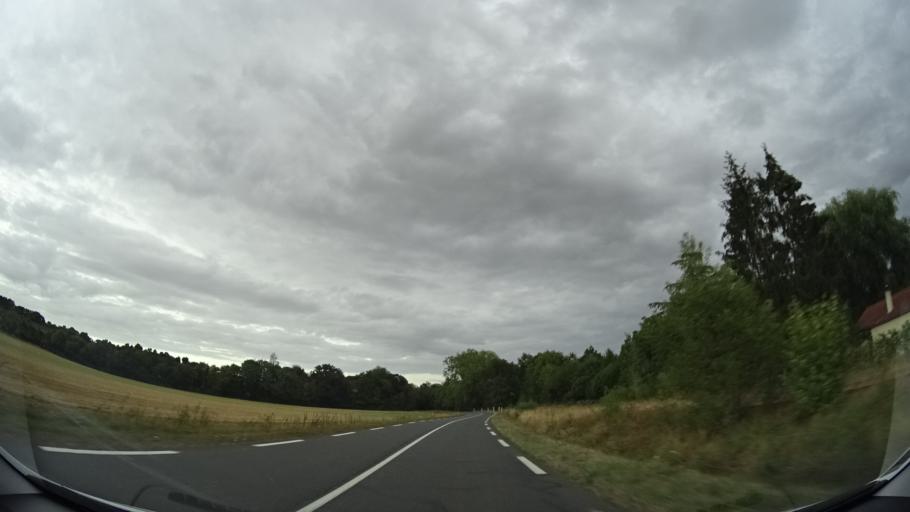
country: FR
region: Centre
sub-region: Departement du Loiret
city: Trigueres
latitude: 47.9362
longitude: 2.9609
